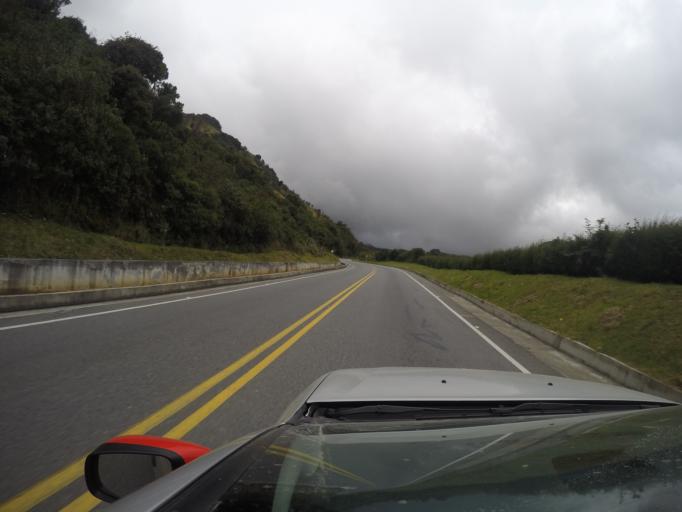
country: CO
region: Caldas
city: Villamaria
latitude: 5.0158
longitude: -75.3404
